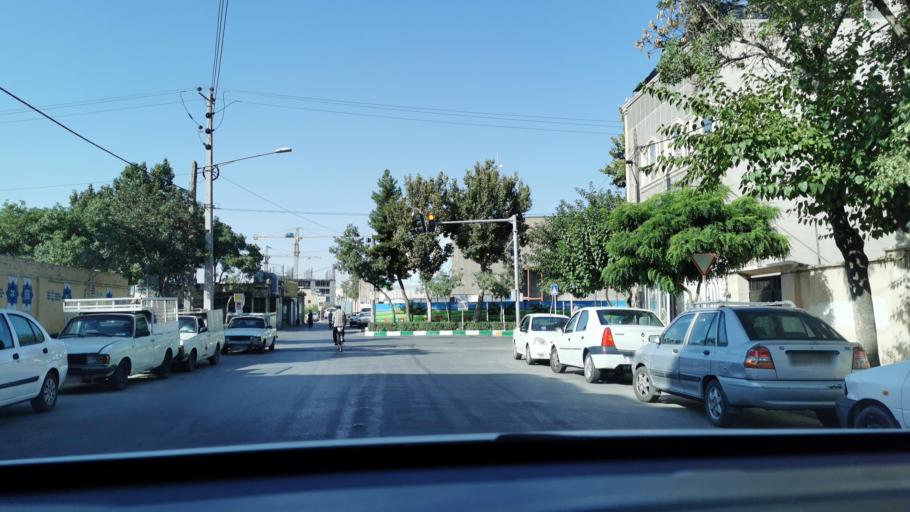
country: IR
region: Razavi Khorasan
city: Mashhad
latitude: 36.2989
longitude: 59.6199
